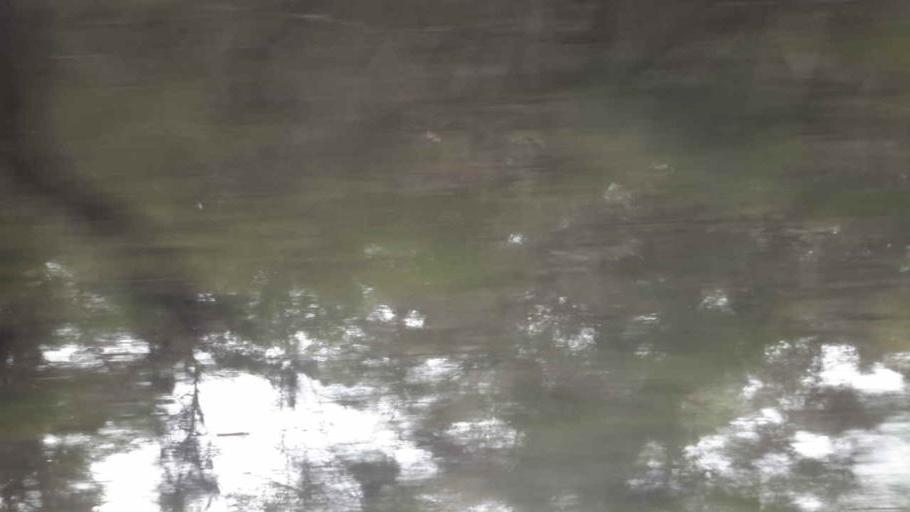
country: AU
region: New South Wales
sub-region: Penrith Municipality
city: Werrington Downs
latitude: -33.7067
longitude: 150.7236
